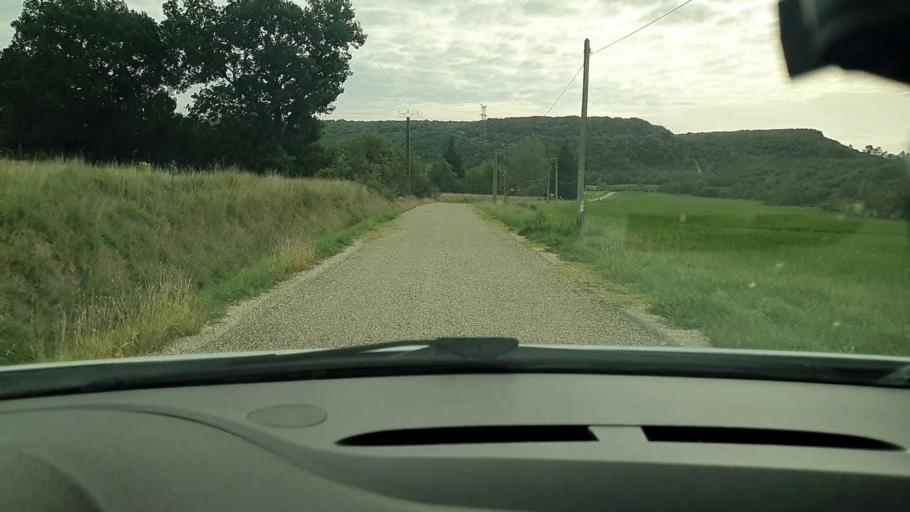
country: FR
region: Languedoc-Roussillon
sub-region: Departement du Gard
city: Montaren-et-Saint-Mediers
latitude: 44.1019
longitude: 4.3125
